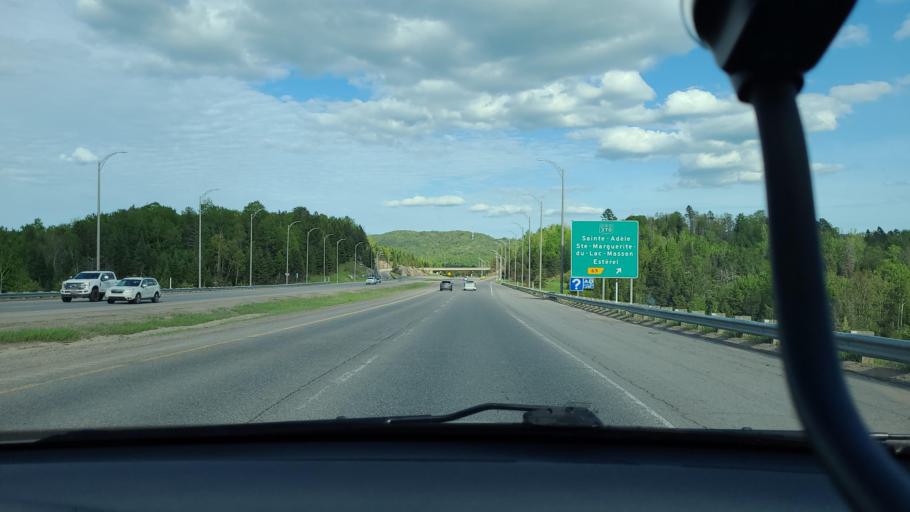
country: CA
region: Quebec
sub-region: Laurentides
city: Sainte-Adele
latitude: 45.9606
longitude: -74.1394
